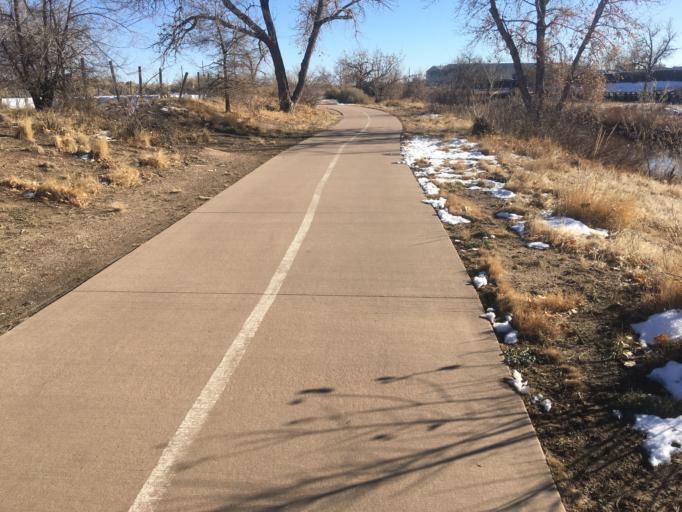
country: US
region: Colorado
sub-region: Adams County
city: Commerce City
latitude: 39.8006
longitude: -104.9381
